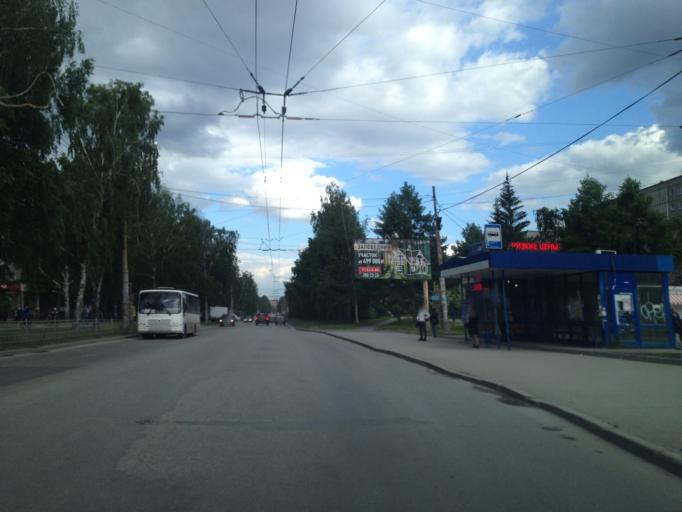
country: RU
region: Sverdlovsk
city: Sovkhoznyy
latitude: 56.8020
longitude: 60.5678
